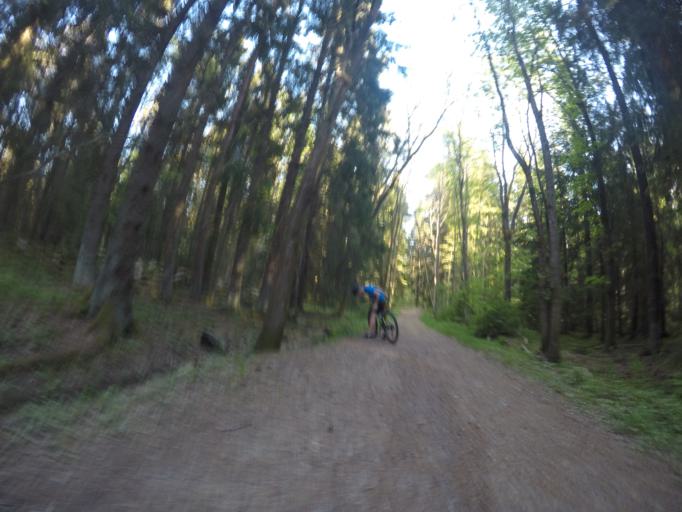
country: SE
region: Soedermanland
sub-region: Eskilstuna Kommun
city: Eskilstuna
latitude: 59.3512
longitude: 16.5216
